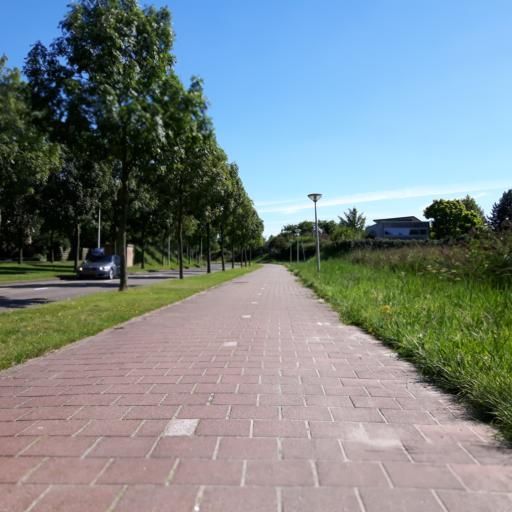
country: NL
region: North Brabant
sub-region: Gemeente Bergen op Zoom
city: Bergen op Zoom
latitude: 51.4738
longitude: 4.2723
